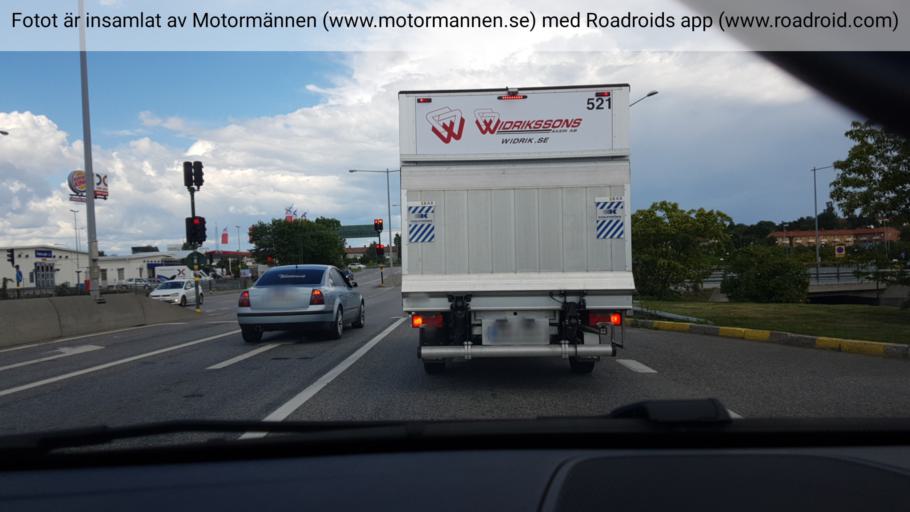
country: SE
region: Stockholm
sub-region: Stockholms Kommun
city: Arsta
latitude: 59.2943
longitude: 18.0347
